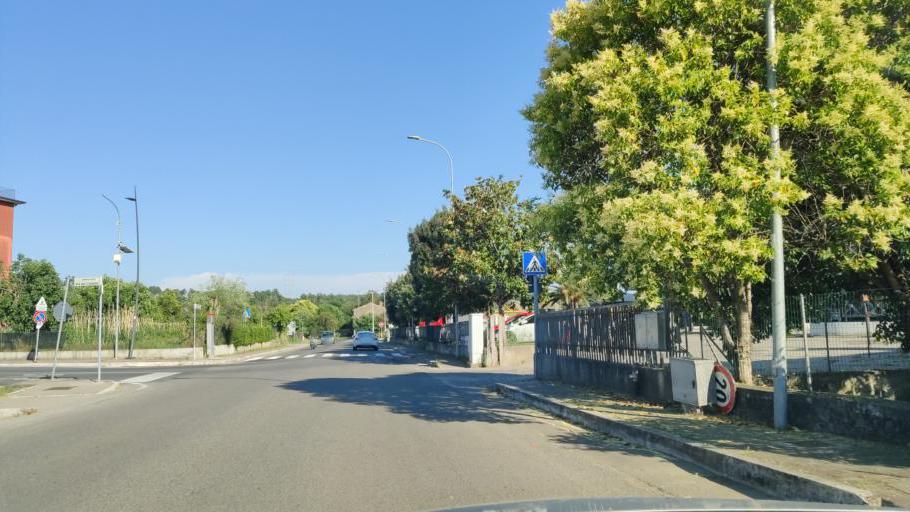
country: IT
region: Latium
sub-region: Provincia di Viterbo
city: Orte
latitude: 42.4663
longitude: 12.3930
